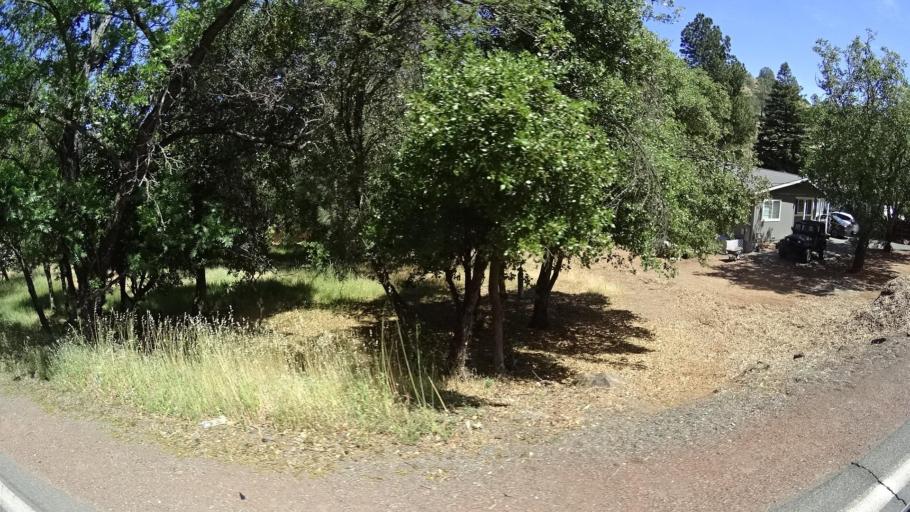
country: US
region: California
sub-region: Lake County
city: Soda Bay
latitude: 38.9543
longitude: -122.7210
